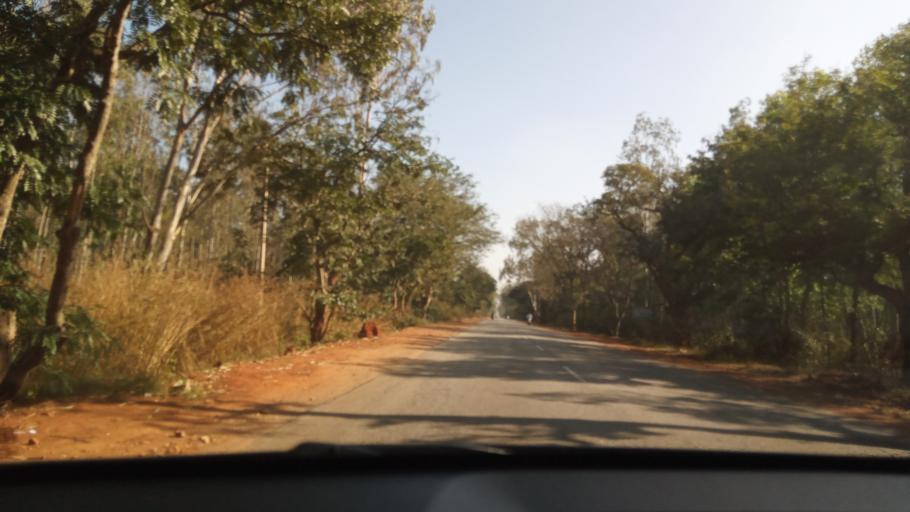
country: IN
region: Karnataka
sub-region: Bangalore Rural
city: Devanhalli
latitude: 13.2708
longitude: 77.7478
